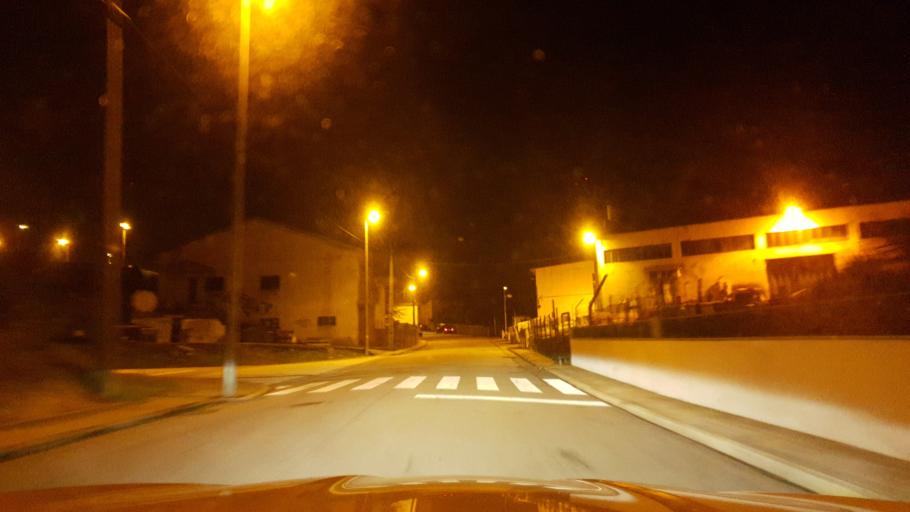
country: PT
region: Porto
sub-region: Matosinhos
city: Senhora da Hora
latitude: 41.2067
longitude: -8.6426
